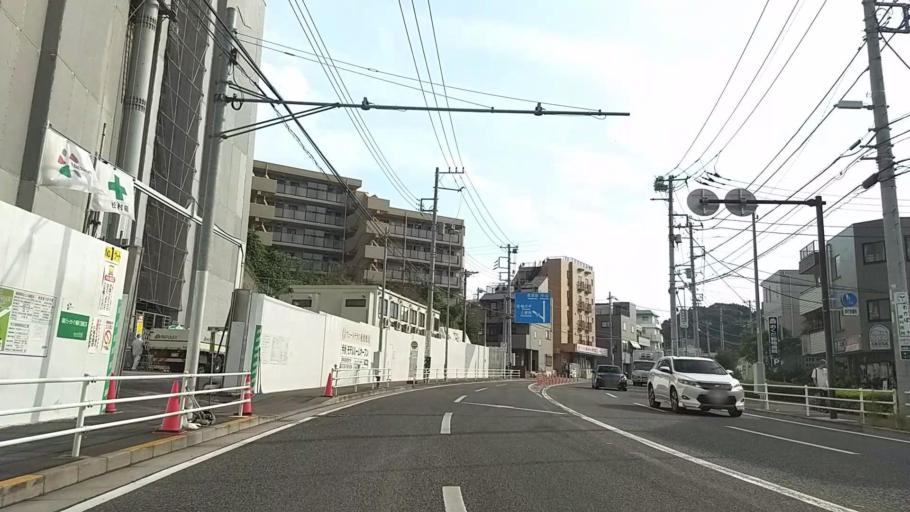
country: JP
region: Kanagawa
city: Yokohama
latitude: 35.5062
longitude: 139.5643
